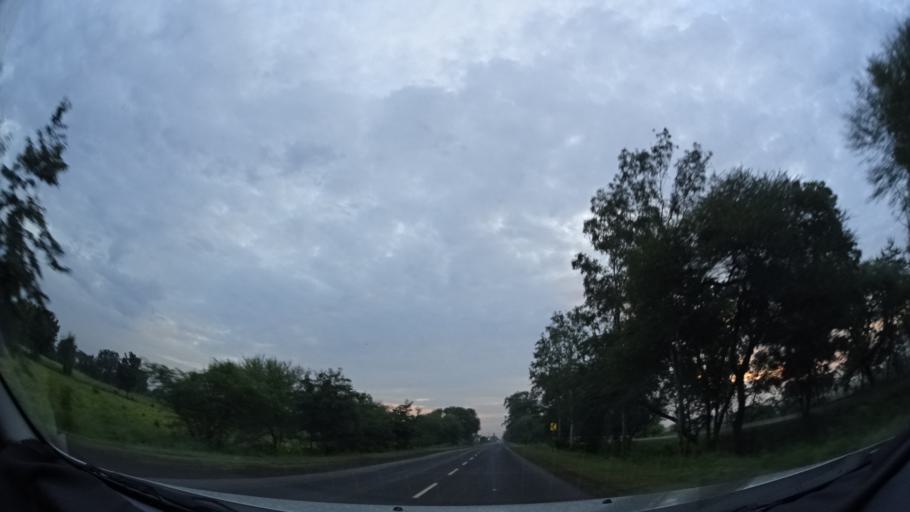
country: IN
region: Madhya Pradesh
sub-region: Dewas
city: Dewas
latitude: 22.9748
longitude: 76.2355
